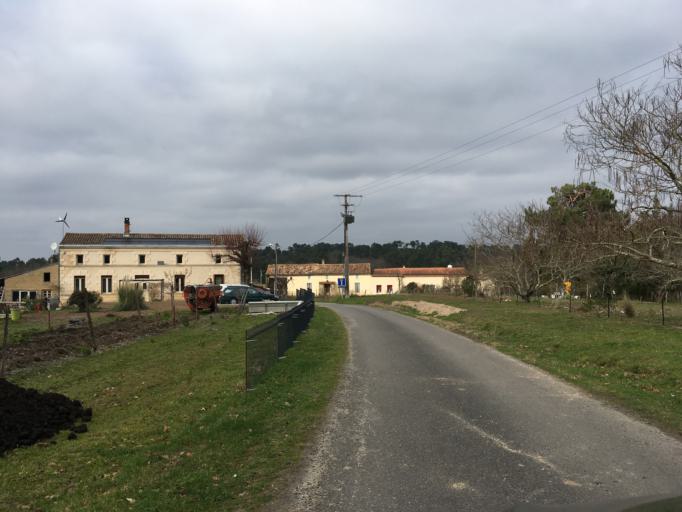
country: FR
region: Aquitaine
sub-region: Departement de la Gironde
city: Saint-Ciers-sur-Gironde
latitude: 45.3211
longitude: -0.6047
